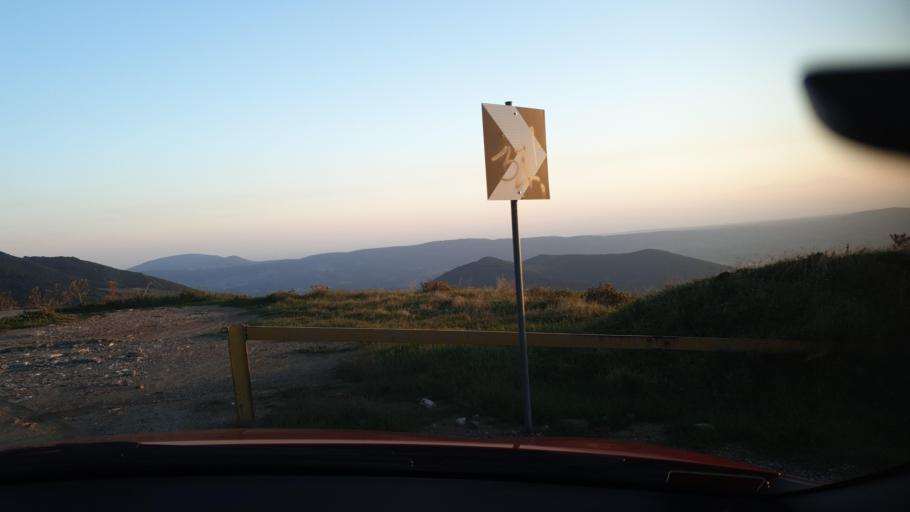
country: GR
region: Central Macedonia
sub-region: Nomos Thessalonikis
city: Peristera
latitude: 40.5195
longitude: 23.2033
